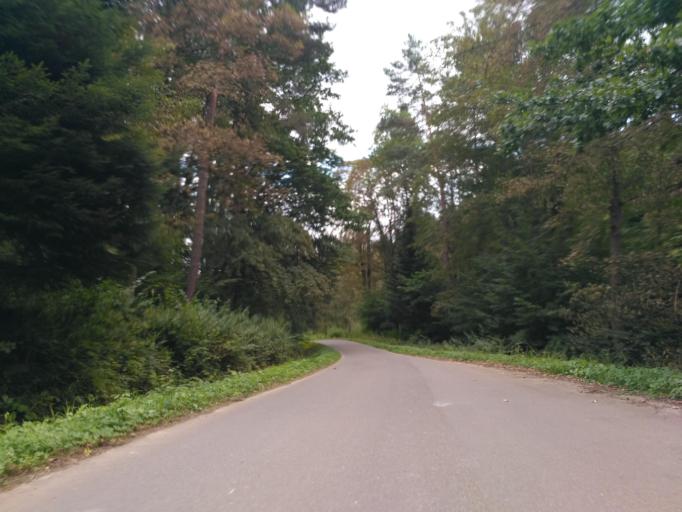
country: PL
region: Subcarpathian Voivodeship
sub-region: Powiat rzeszowski
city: Dynow
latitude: 49.7599
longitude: 22.2826
